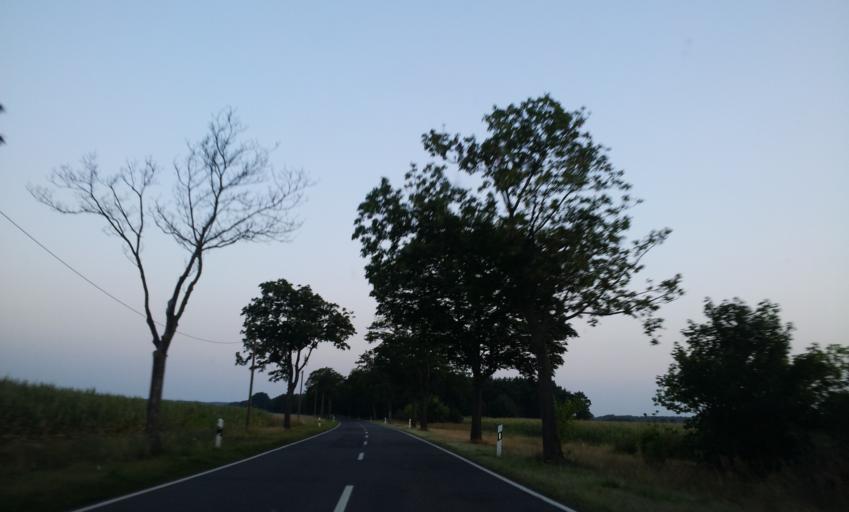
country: DE
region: Brandenburg
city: Treuenbrietzen
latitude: 52.1011
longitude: 12.9496
